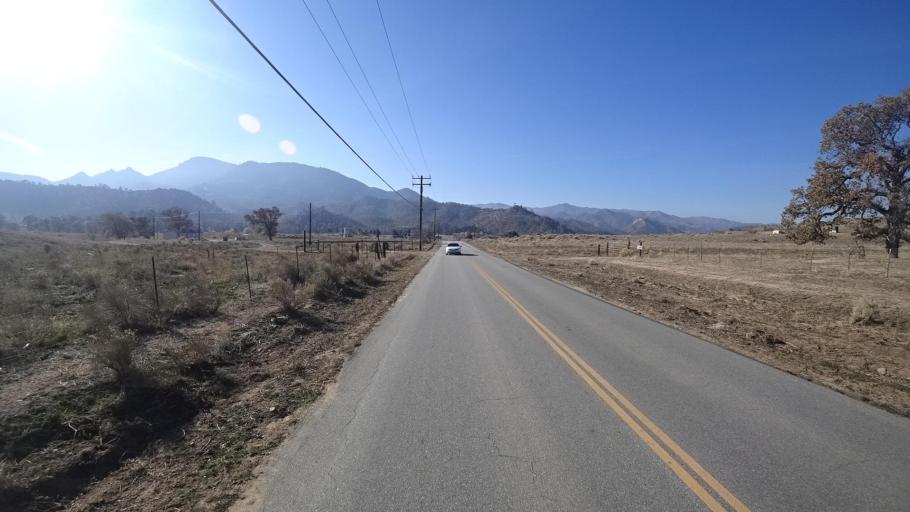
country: US
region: California
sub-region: Kern County
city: Tehachapi
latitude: 35.3205
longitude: -118.3916
